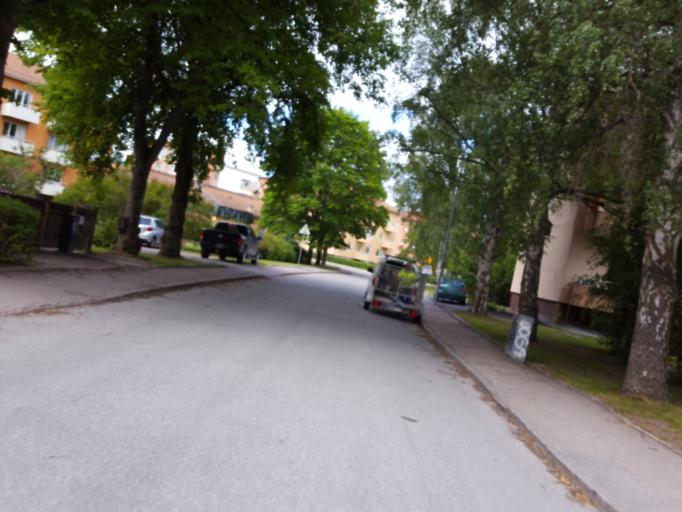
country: SE
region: Uppsala
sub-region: Uppsala Kommun
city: Uppsala
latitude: 59.8464
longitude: 17.6340
